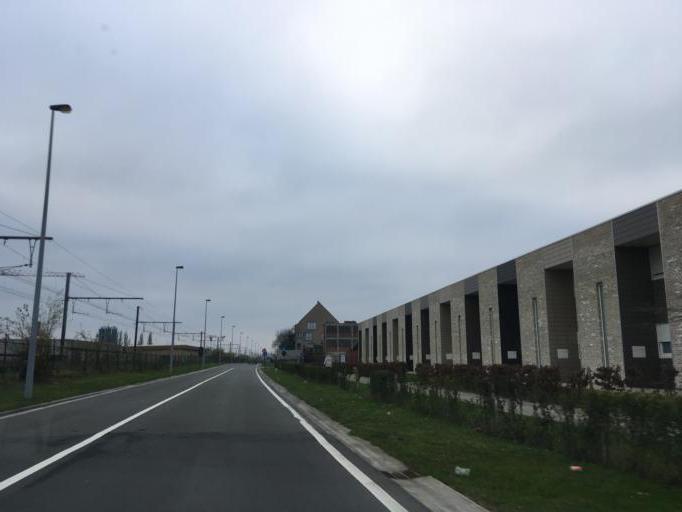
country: BE
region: Flanders
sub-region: Provincie West-Vlaanderen
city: Roeselare
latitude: 50.9598
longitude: 3.1271
